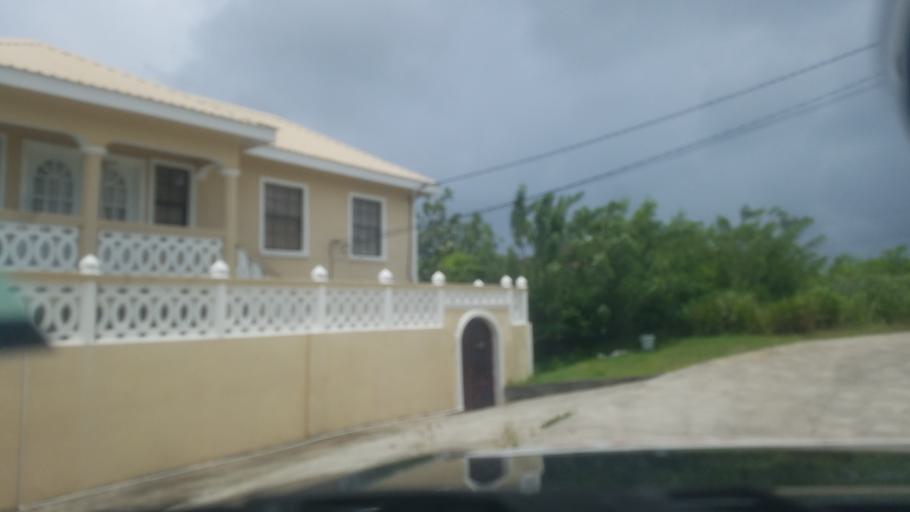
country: LC
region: Laborie Quarter
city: Laborie
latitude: 13.7584
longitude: -60.9723
